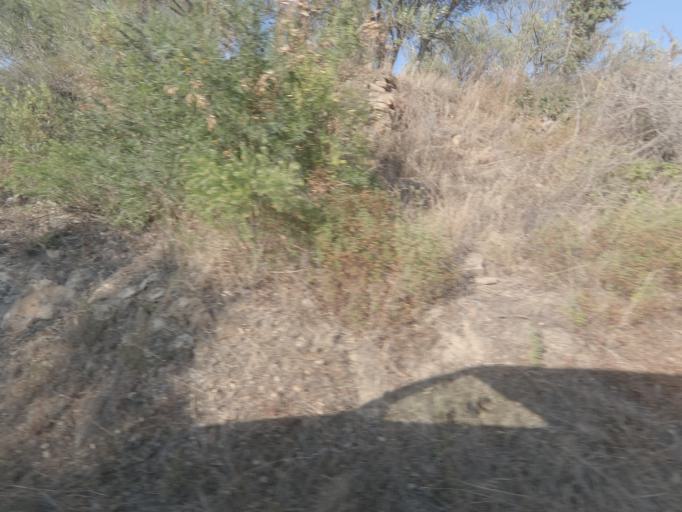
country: PT
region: Vila Real
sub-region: Sabrosa
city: Sabrosa
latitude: 41.2641
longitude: -7.5407
